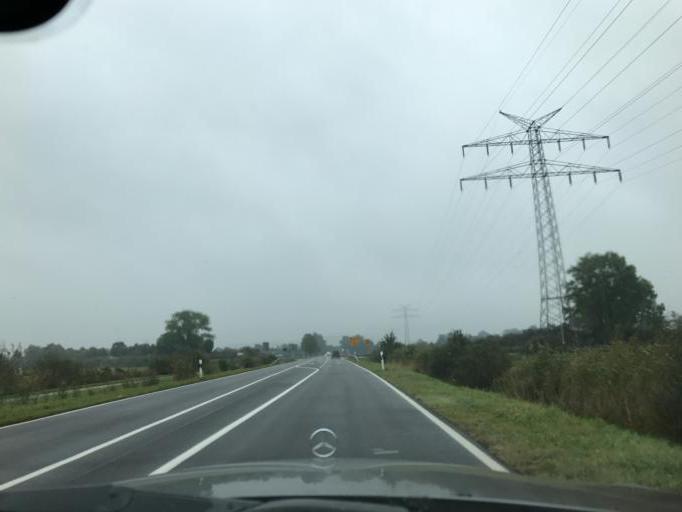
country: DE
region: Lower Saxony
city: Weener
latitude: 53.1146
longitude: 7.3449
